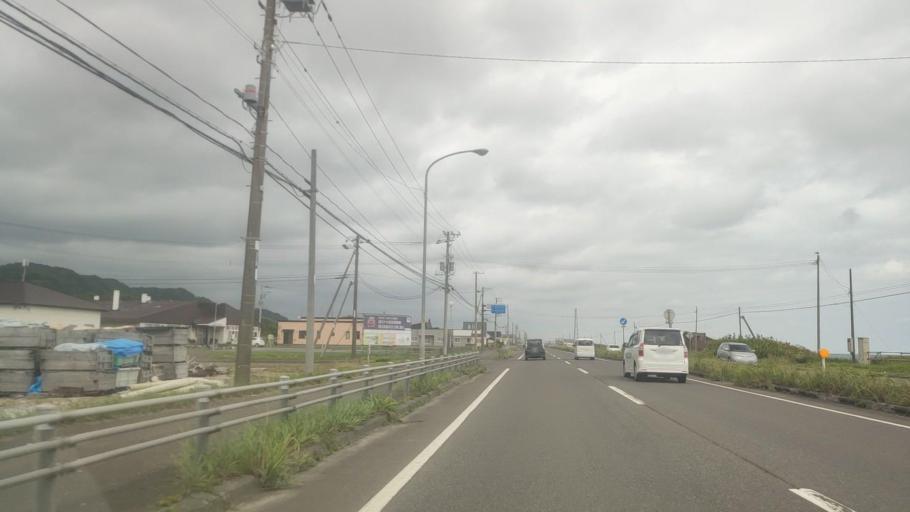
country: JP
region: Hokkaido
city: Shiraoi
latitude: 42.4655
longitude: 141.2228
